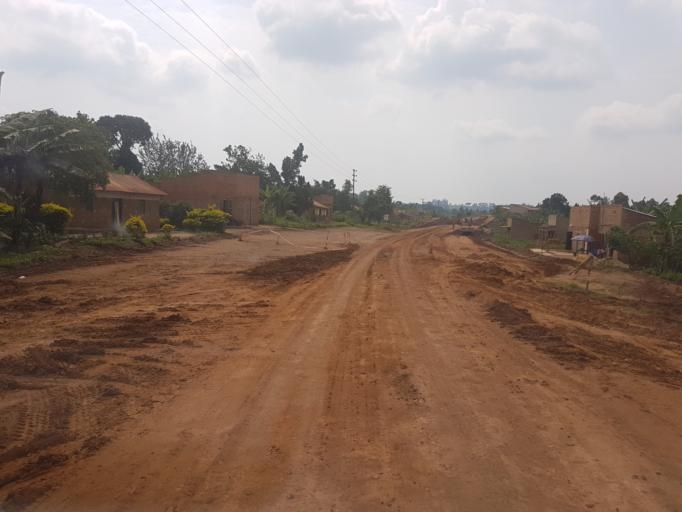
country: UG
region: Western Region
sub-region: Kanungu District
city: Ntungamo
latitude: -0.8040
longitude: 29.7034
